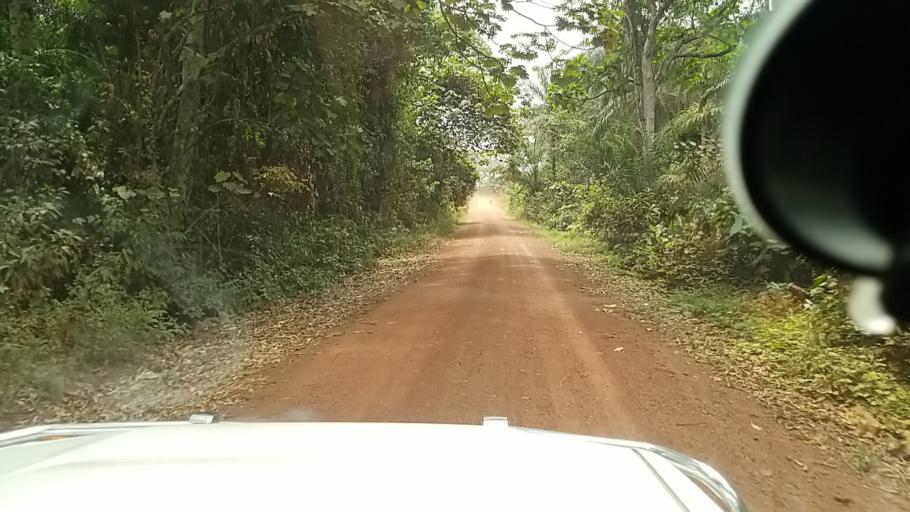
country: CD
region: Equateur
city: Libenge
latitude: 3.7456
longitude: 18.7853
